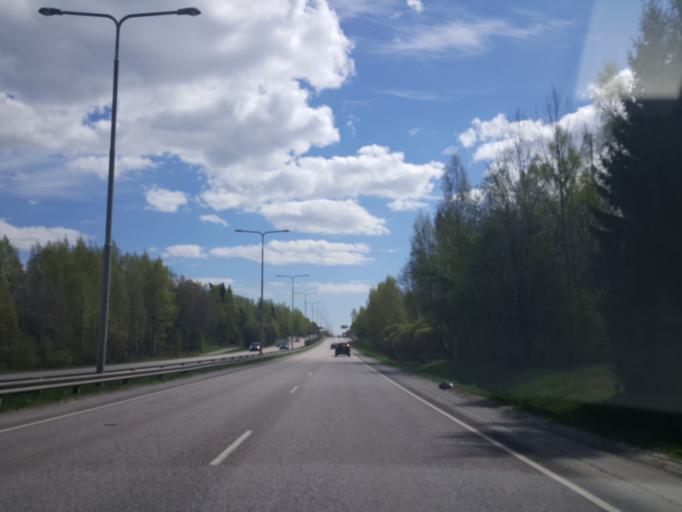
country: FI
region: Uusimaa
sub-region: Helsinki
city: Teekkarikylae
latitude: 60.2506
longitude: 24.8854
